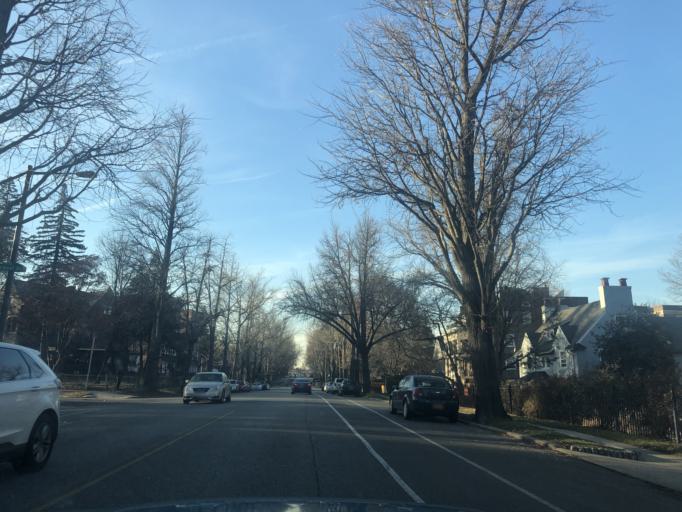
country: US
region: Pennsylvania
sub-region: Delaware County
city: Millbourne
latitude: 39.9859
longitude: -75.2490
